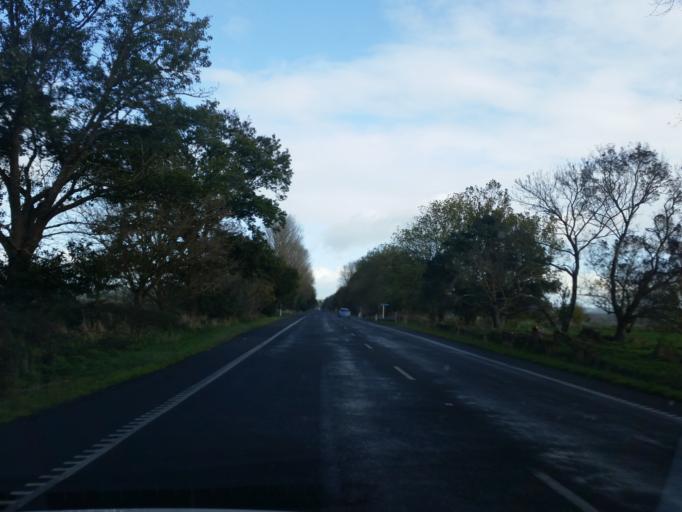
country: NZ
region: Waikato
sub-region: Hauraki District
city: Ngatea
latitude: -37.2796
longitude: 175.4401
